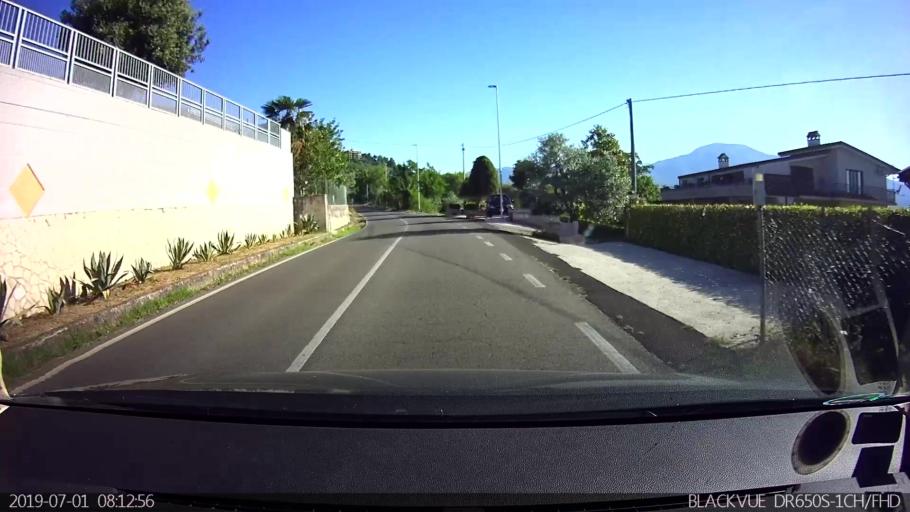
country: IT
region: Latium
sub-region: Provincia di Frosinone
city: Veroli
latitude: 41.6865
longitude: 13.4229
